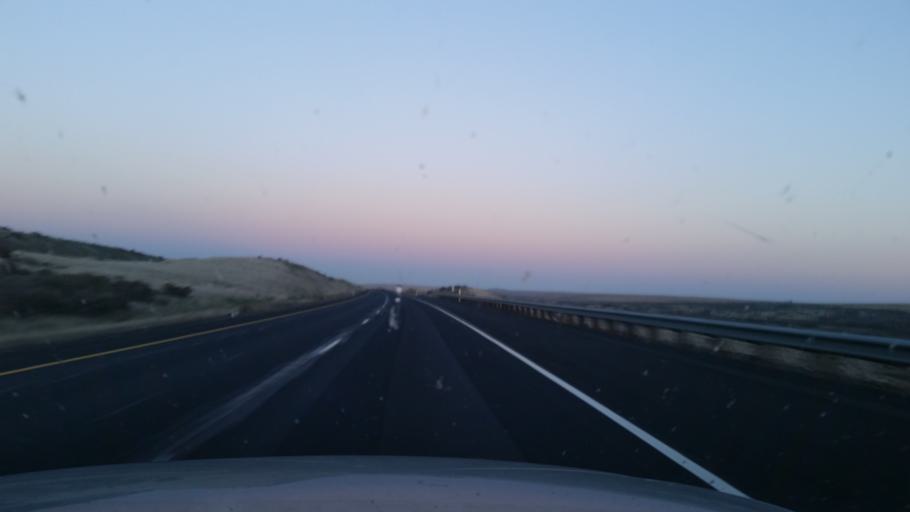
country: US
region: Washington
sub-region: Adams County
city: Ritzville
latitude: 47.0968
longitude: -118.6242
